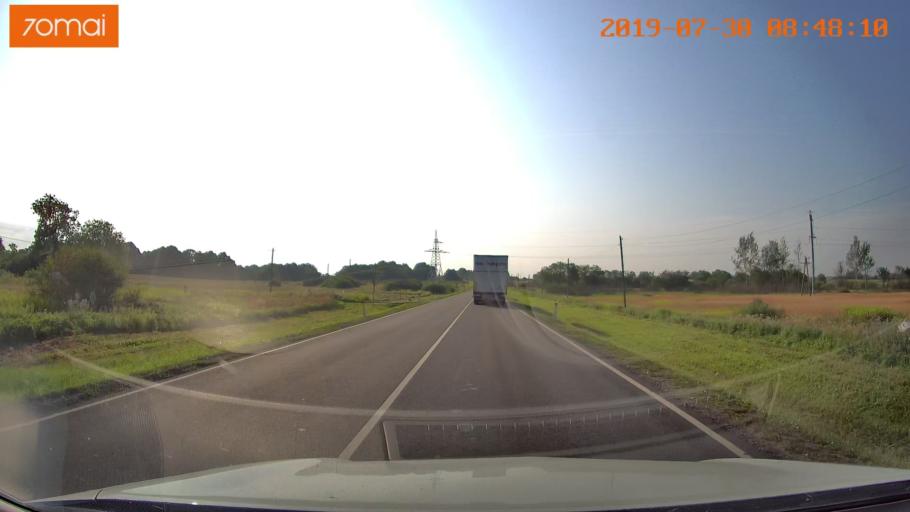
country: RU
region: Kaliningrad
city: Chernyakhovsk
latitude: 54.6193
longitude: 21.9016
